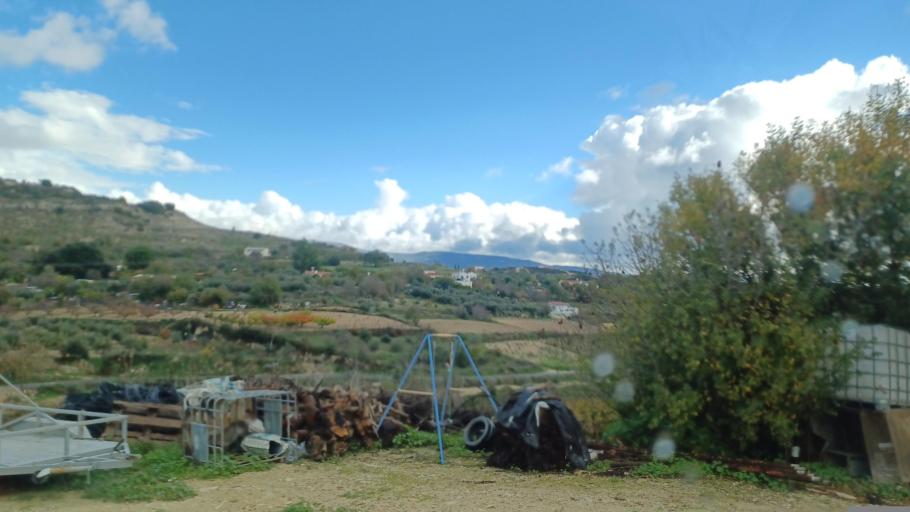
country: CY
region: Pafos
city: Mesogi
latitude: 34.8520
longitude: 32.5153
